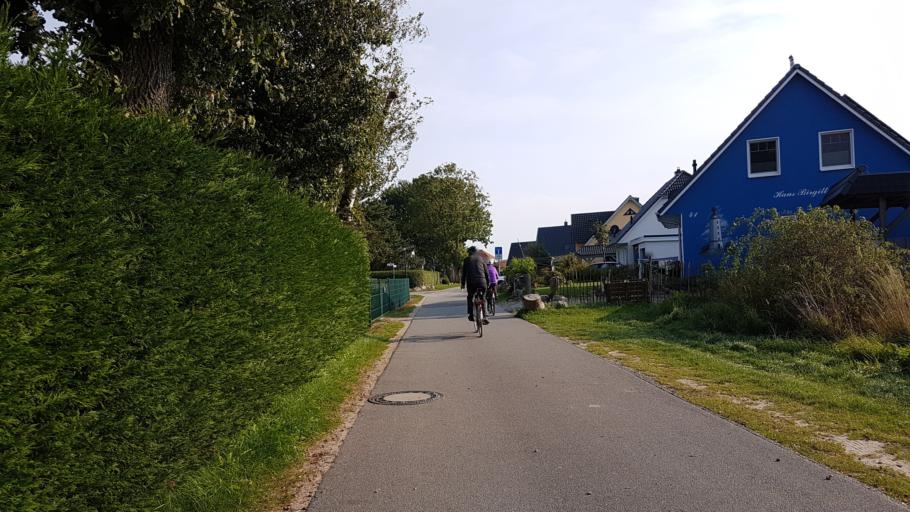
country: DE
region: Mecklenburg-Vorpommern
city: Glowe
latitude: 54.5675
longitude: 13.4739
